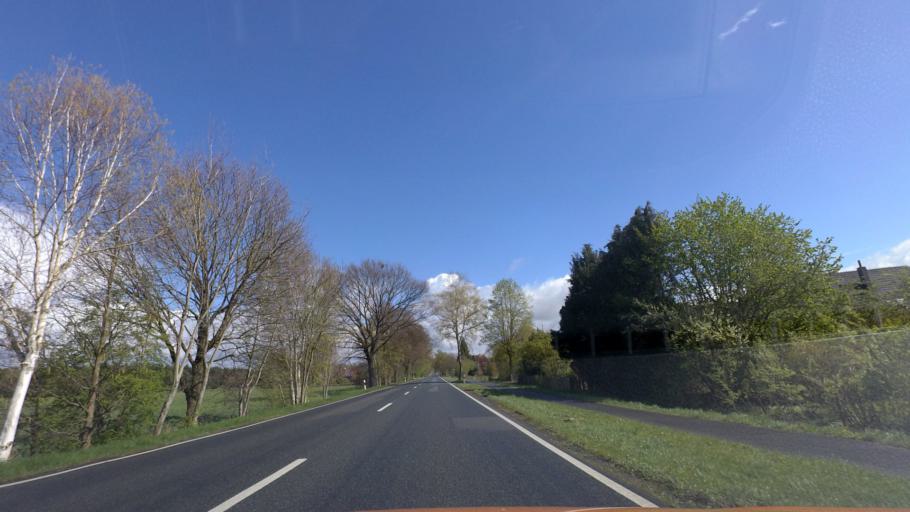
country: DE
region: Lower Saxony
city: Ottersberg
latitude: 53.0782
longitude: 9.1057
